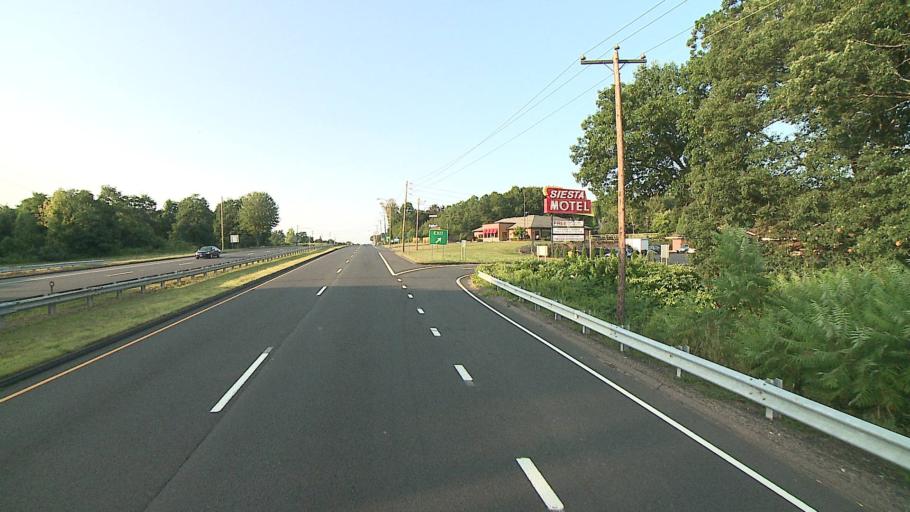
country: US
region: Connecticut
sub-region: Hartford County
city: Newington
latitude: 41.6977
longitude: -72.7047
